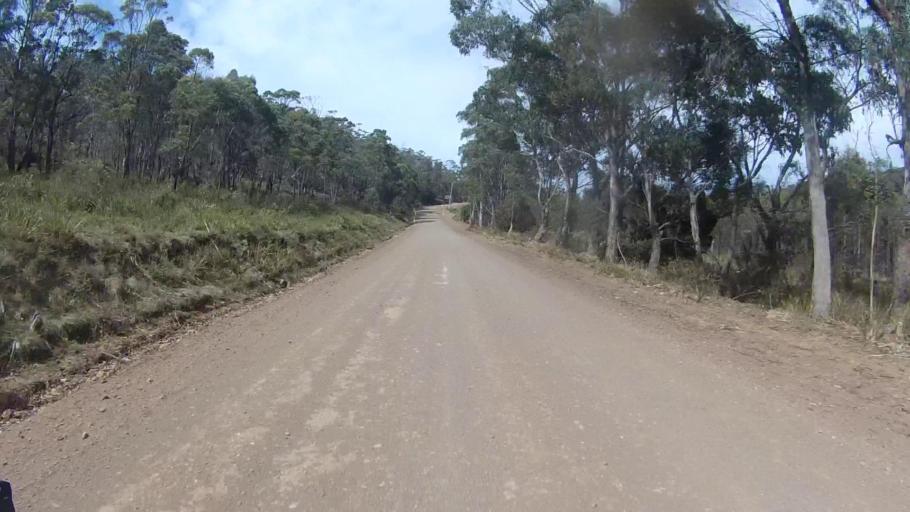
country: AU
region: Tasmania
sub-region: Sorell
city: Sorell
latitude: -42.6658
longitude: 147.8884
